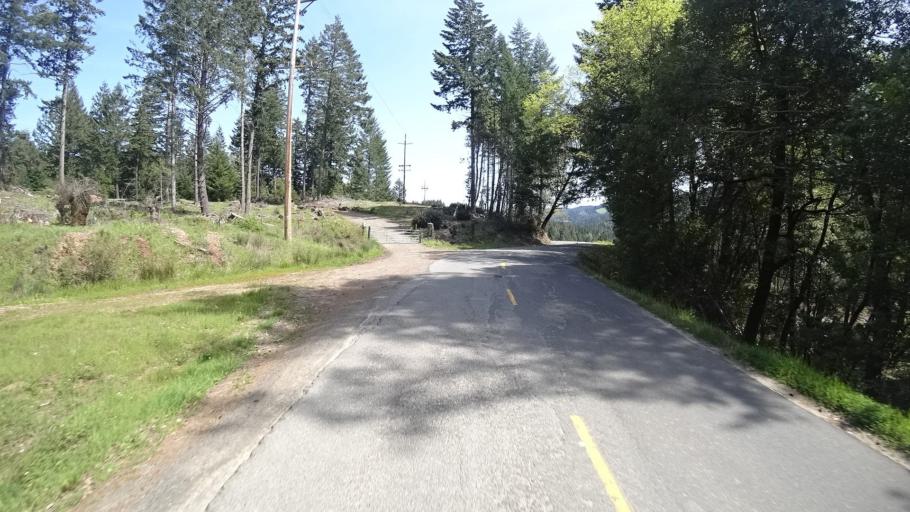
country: US
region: California
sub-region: Humboldt County
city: Redway
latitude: 40.3694
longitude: -123.7346
